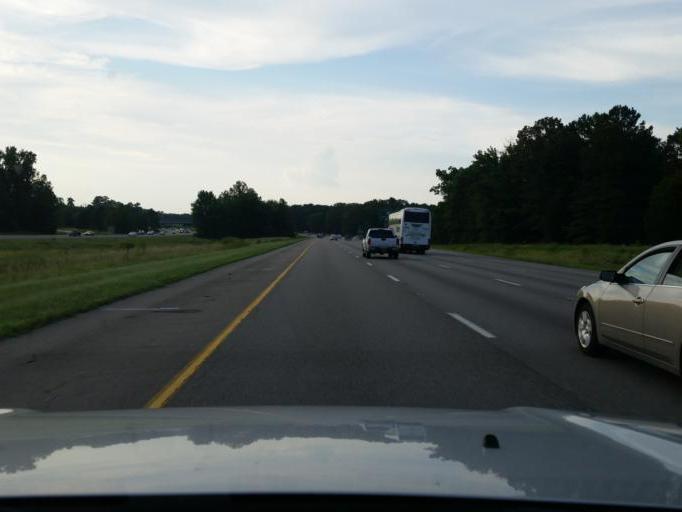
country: US
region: Virginia
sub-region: Hanover County
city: Mechanicsville
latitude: 37.6232
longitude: -77.3676
